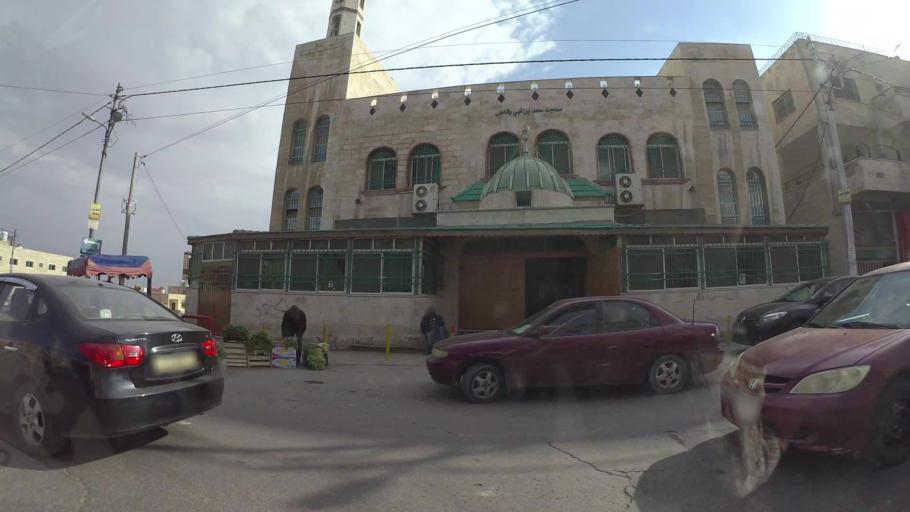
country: JO
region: Amman
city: Amman
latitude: 31.9976
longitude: 35.9467
